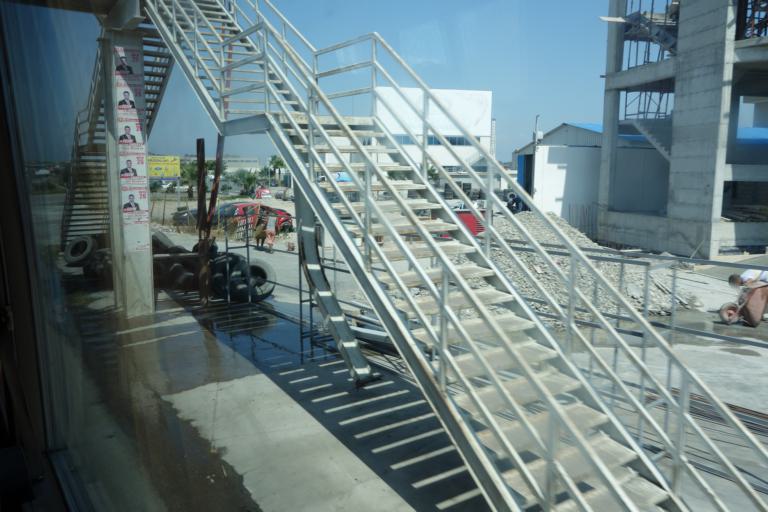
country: AL
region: Durres
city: Durres
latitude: 41.3284
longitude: 19.4734
